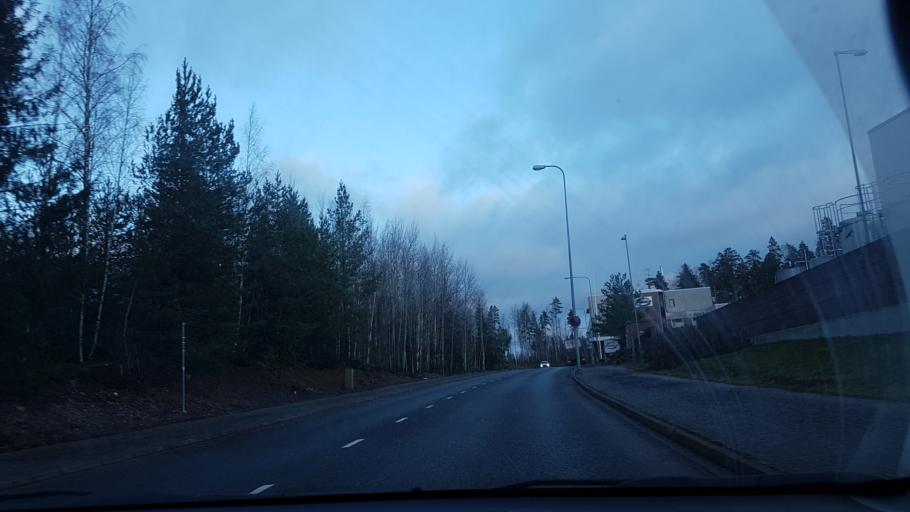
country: FI
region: Uusimaa
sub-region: Helsinki
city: Kilo
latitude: 60.3092
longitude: 24.8522
